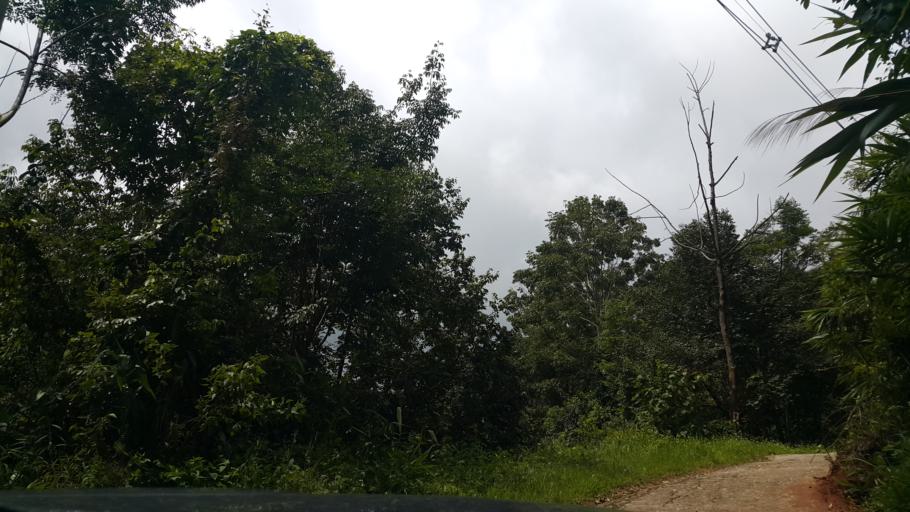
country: TH
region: Lampang
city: Wang Nuea
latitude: 19.0953
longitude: 99.3687
